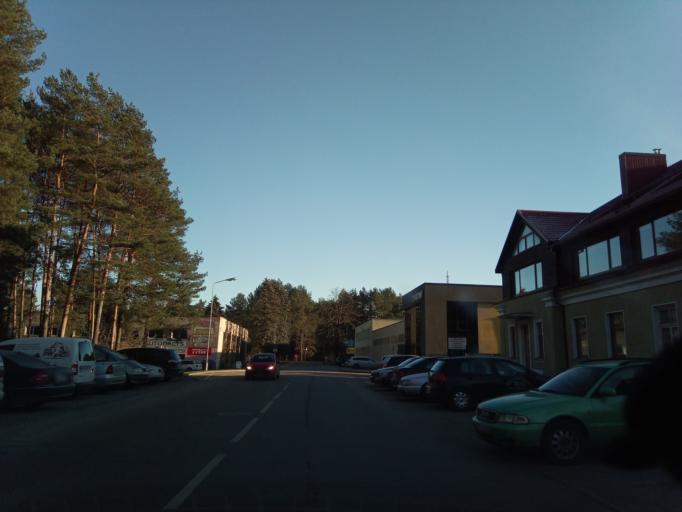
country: LT
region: Alytaus apskritis
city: Druskininkai
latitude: 54.0026
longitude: 23.9794
